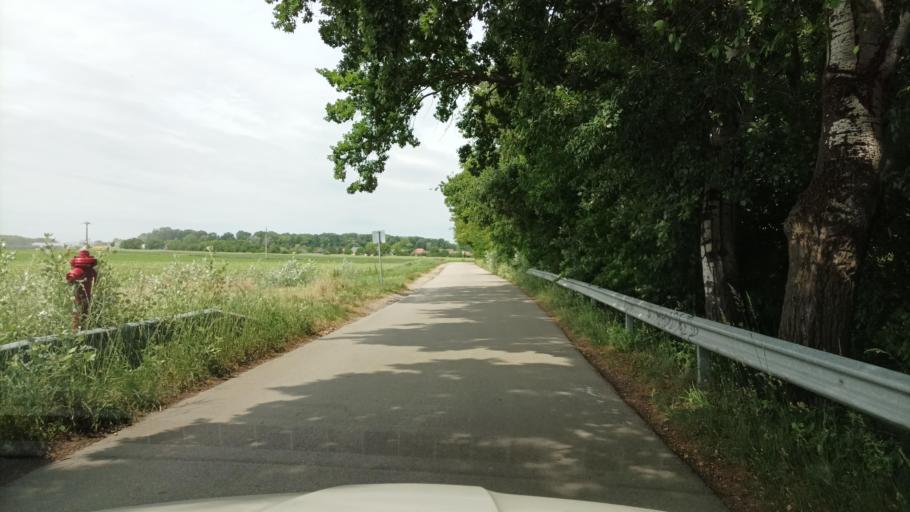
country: HU
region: Pest
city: Rackeve
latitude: 47.1247
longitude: 18.9582
